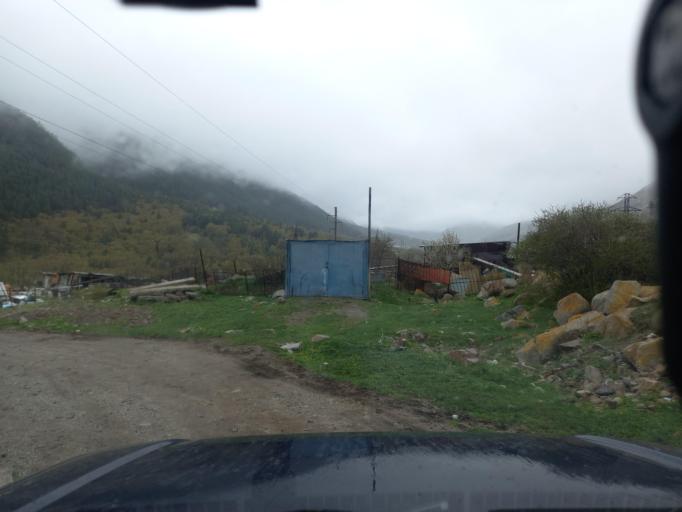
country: RU
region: Kabardino-Balkariya
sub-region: El'brusskiy Rayon
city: El'brus
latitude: 43.2771
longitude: 42.6838
